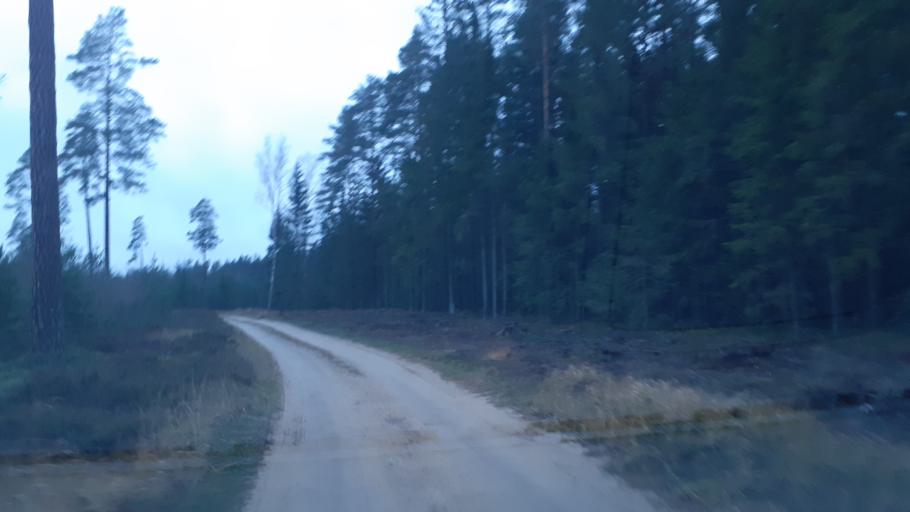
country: LV
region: Kuldigas Rajons
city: Kuldiga
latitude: 56.9961
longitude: 22.0519
